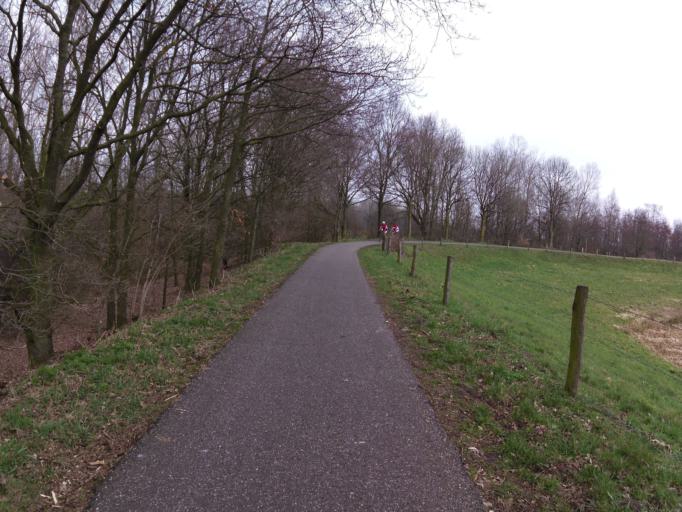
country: NL
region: North Brabant
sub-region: Gemeente Heusden
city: Heusden
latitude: 51.7064
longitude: 5.1126
